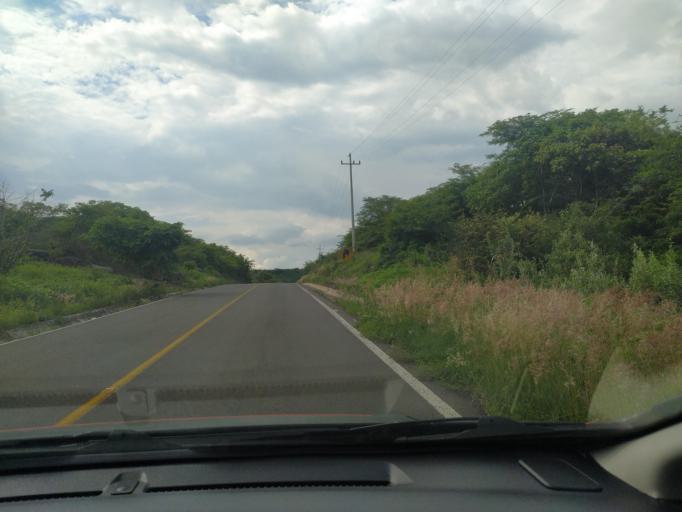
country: MX
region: Jalisco
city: Villa Corona
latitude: 20.3770
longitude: -103.6717
